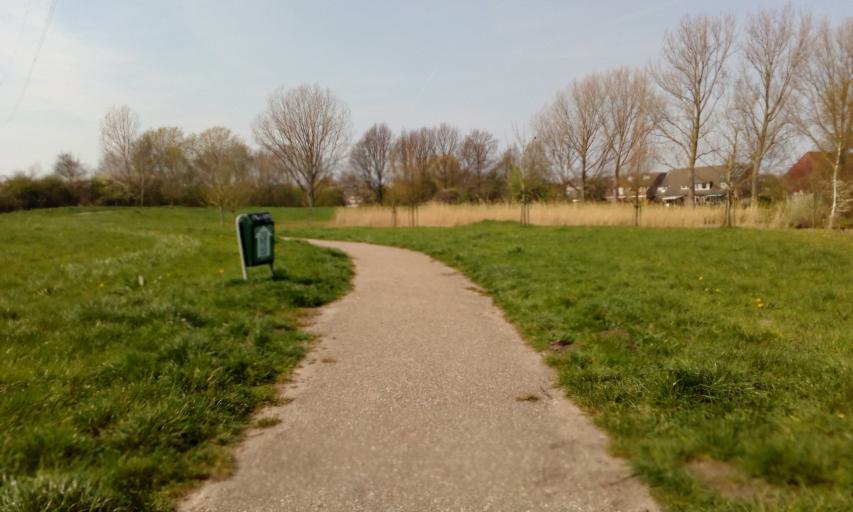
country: NL
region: South Holland
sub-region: Gemeente Spijkenisse
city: Spijkenisse
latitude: 51.8288
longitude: 4.3407
